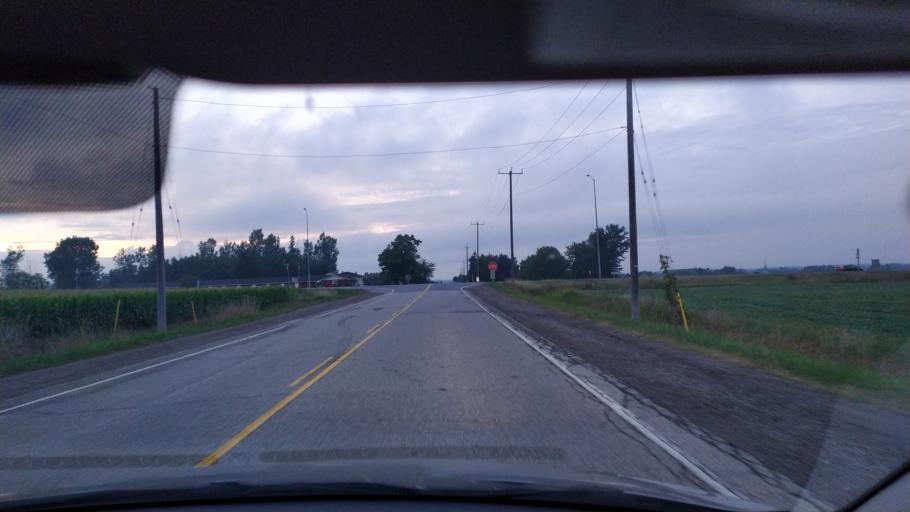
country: CA
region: Ontario
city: Kitchener
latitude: 43.3643
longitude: -80.7110
